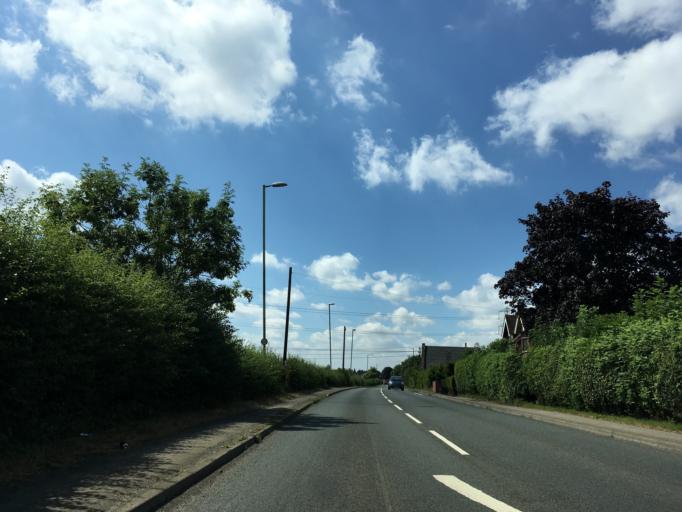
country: GB
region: England
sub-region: Gloucestershire
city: Gloucester
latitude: 51.8924
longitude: -2.2322
